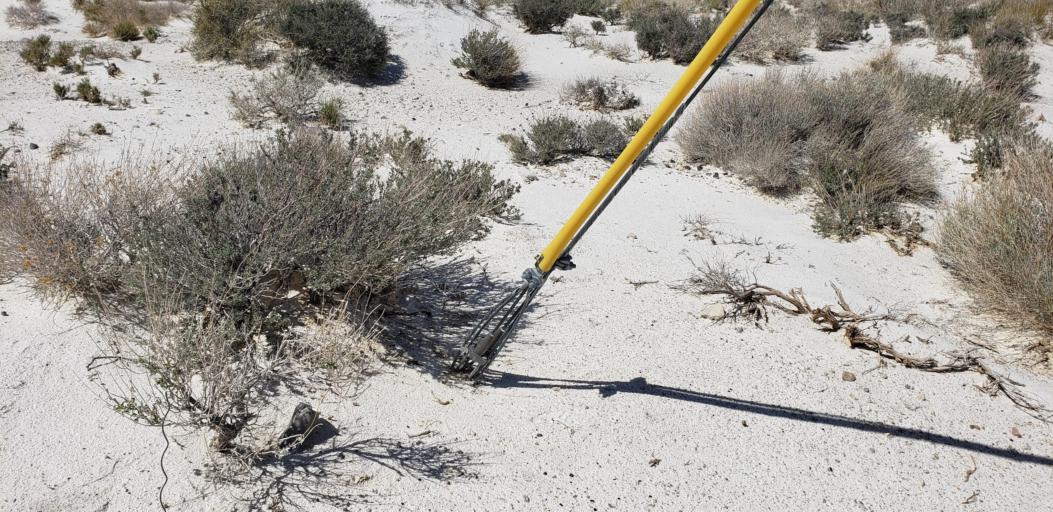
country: US
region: California
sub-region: San Bernardino County
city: Lucerne Valley
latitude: 34.3689
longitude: -116.9071
